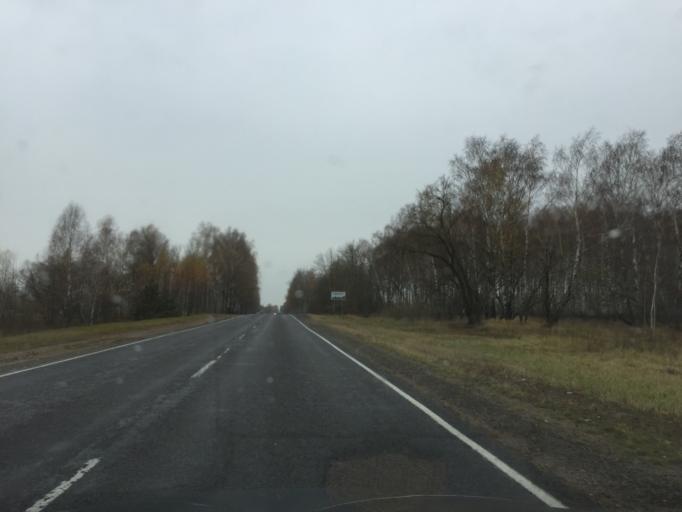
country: BY
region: Mogilev
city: Slawharad
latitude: 53.3483
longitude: 30.8173
